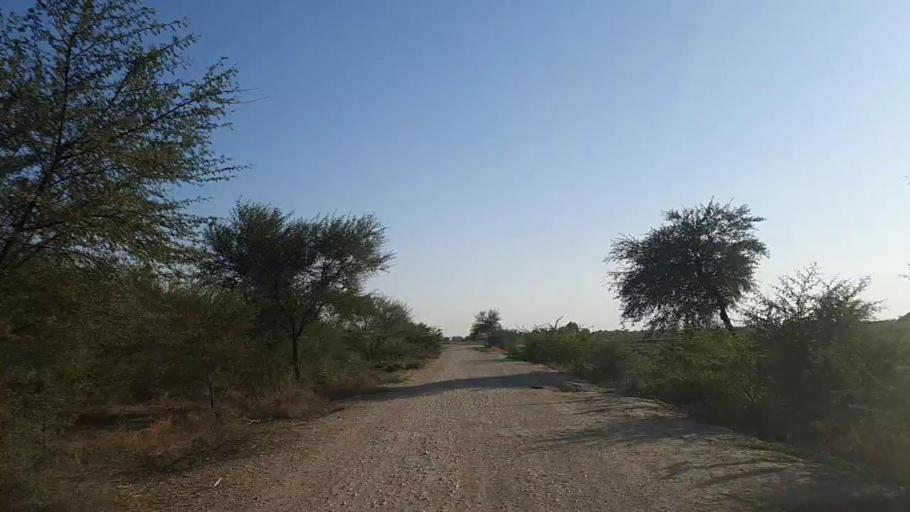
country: PK
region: Sindh
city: Naukot
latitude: 24.9617
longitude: 69.3881
